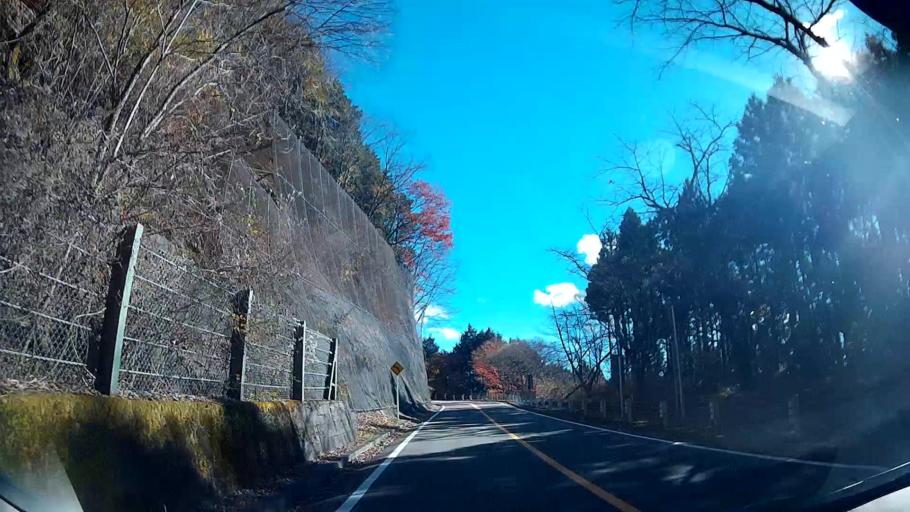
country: JP
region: Yamanashi
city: Uenohara
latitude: 35.7375
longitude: 139.0328
